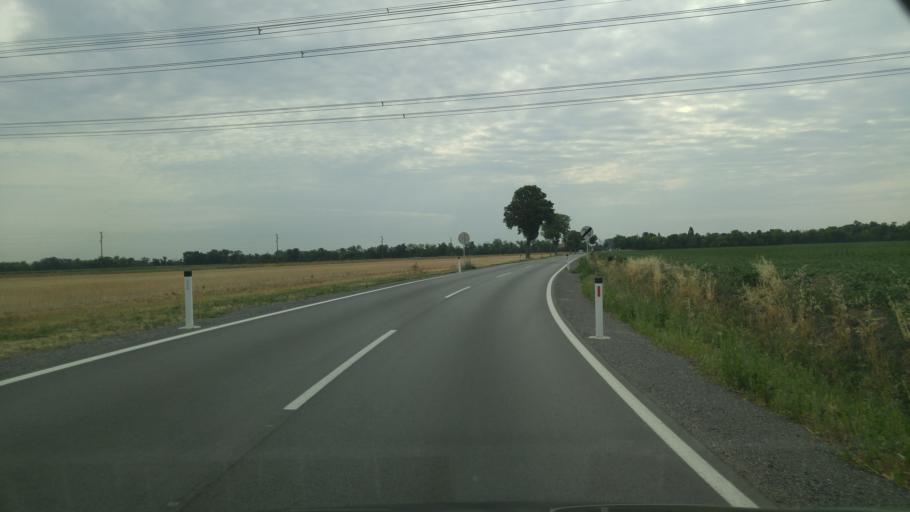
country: AT
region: Lower Austria
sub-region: Politischer Bezirk Modling
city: Munchendorf
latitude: 48.0356
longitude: 16.3925
